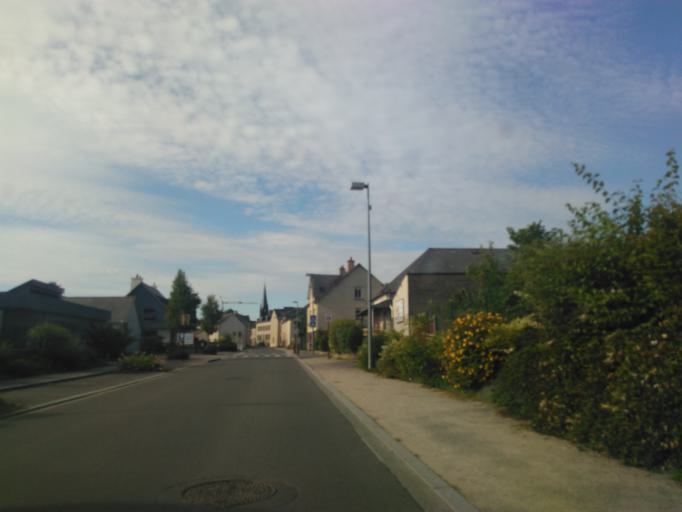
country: FR
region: Brittany
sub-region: Departement d'Ille-et-Vilaine
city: Romille
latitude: 48.2132
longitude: -1.8930
